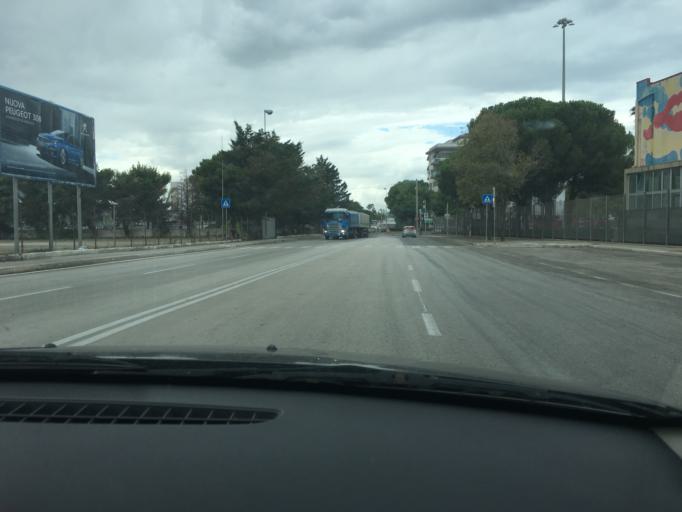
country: IT
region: Apulia
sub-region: Provincia di Bari
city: Bari
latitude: 41.1305
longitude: 16.8394
